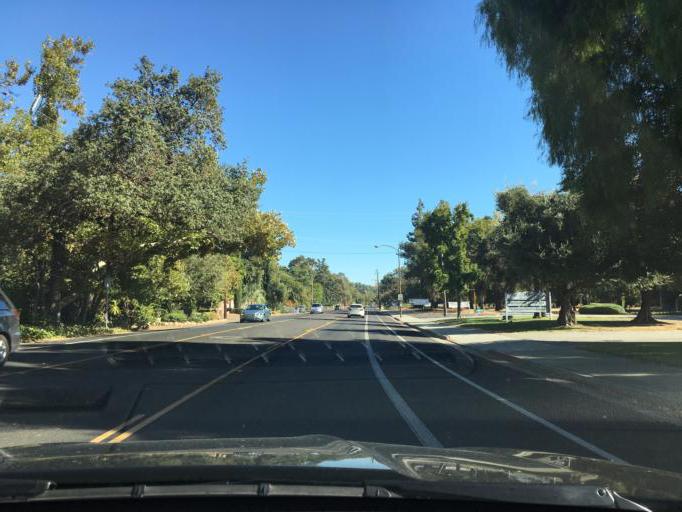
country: US
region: California
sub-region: Santa Clara County
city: Seven Trees
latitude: 37.2234
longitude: -121.8582
